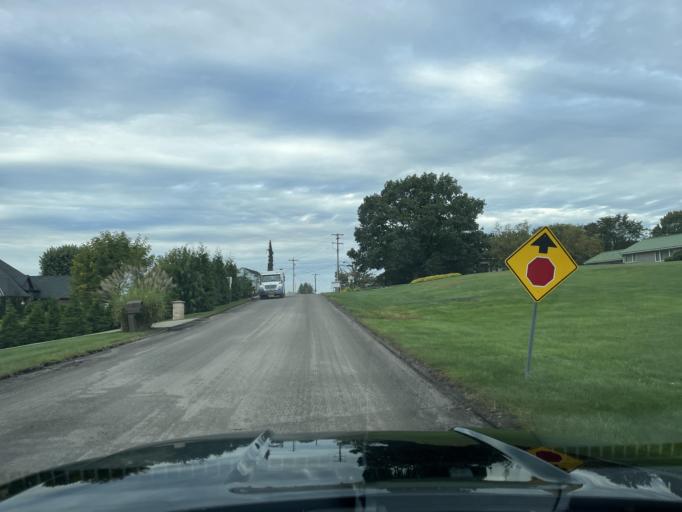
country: US
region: Pennsylvania
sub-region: Fayette County
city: Leith-Hatfield
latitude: 39.8784
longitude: -79.7262
